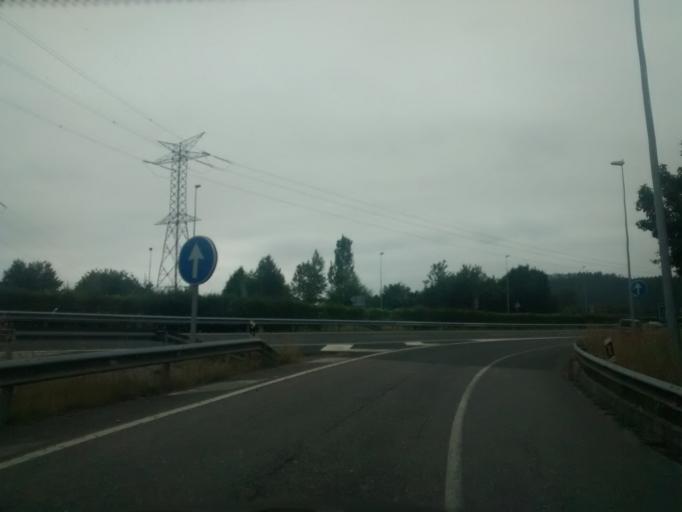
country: ES
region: Cantabria
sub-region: Provincia de Cantabria
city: Luzmela
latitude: 43.3261
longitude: -4.1911
